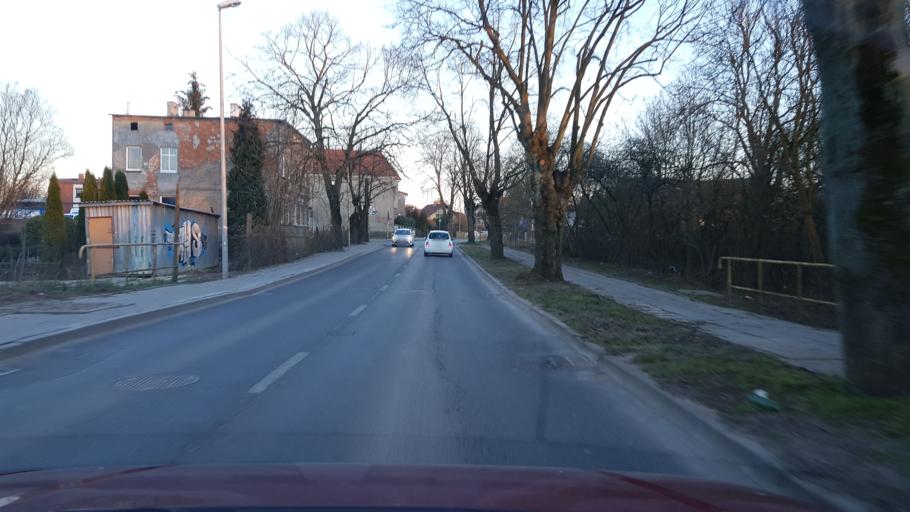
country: PL
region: West Pomeranian Voivodeship
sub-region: Szczecin
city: Szczecin
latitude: 53.4748
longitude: 14.5463
